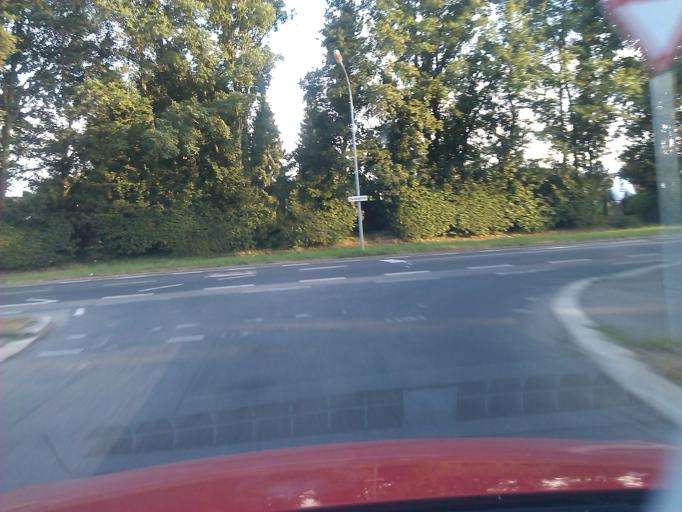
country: DE
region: Baden-Wuerttemberg
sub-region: Regierungsbezirk Stuttgart
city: Heilbronn
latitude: 49.1517
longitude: 9.1876
